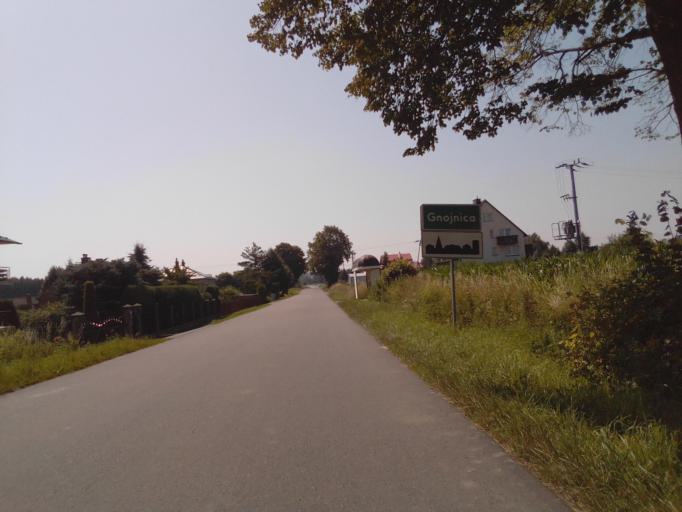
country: PL
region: Subcarpathian Voivodeship
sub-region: Powiat ropczycko-sedziszowski
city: Sedziszow Malopolski
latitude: 50.0644
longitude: 21.6636
